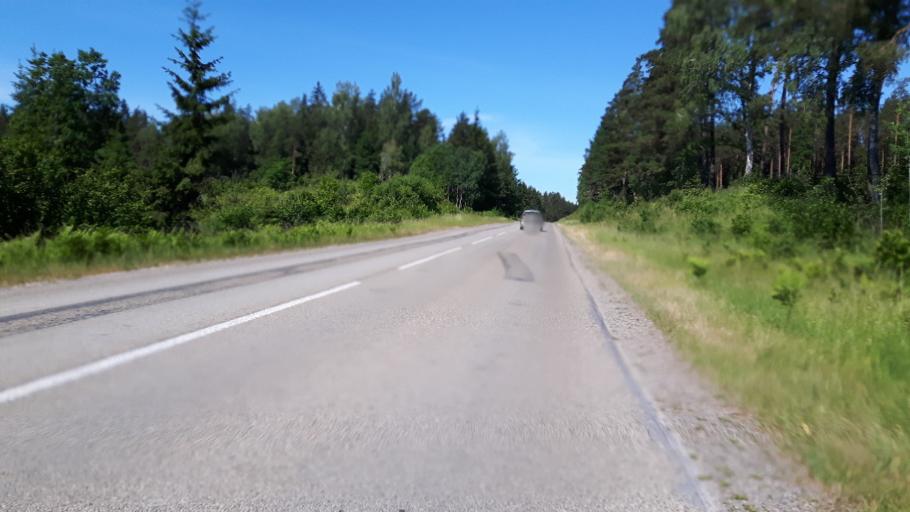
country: LV
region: Tukuma Rajons
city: Tukums
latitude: 57.0049
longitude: 23.0708
